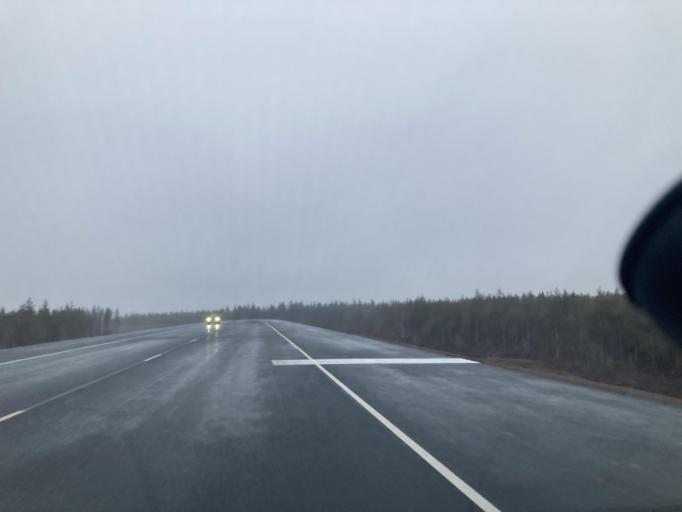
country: FI
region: Lapland
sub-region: Rovaniemi
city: Rovaniemi
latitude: 66.5845
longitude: 25.8011
